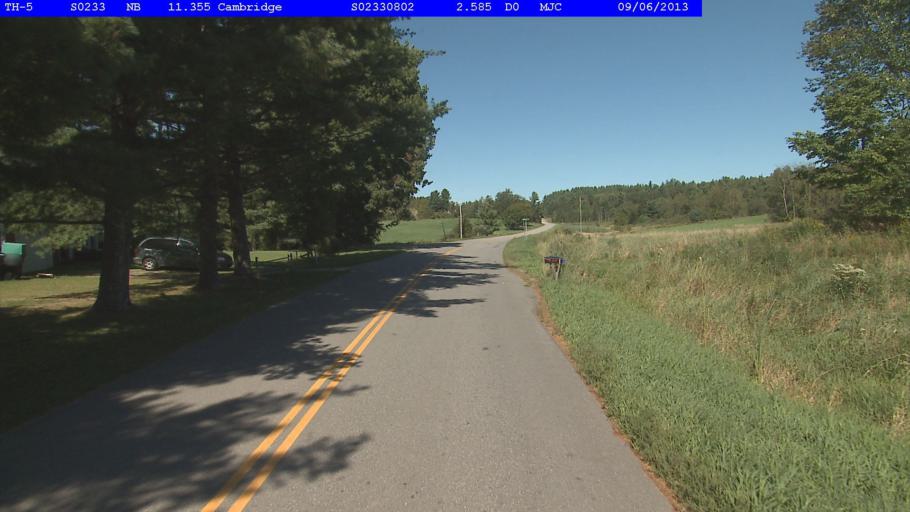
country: US
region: Vermont
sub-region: Lamoille County
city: Johnson
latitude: 44.6188
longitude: -72.8569
